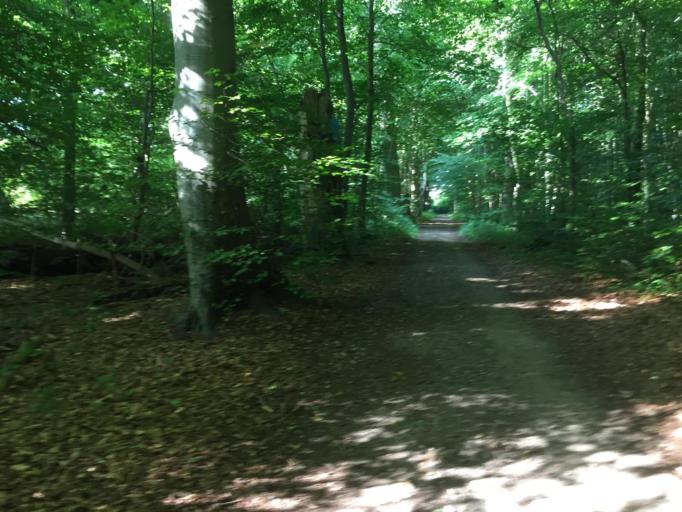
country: DK
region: South Denmark
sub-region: Odense Kommune
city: Hojby
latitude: 55.3493
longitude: 10.4386
